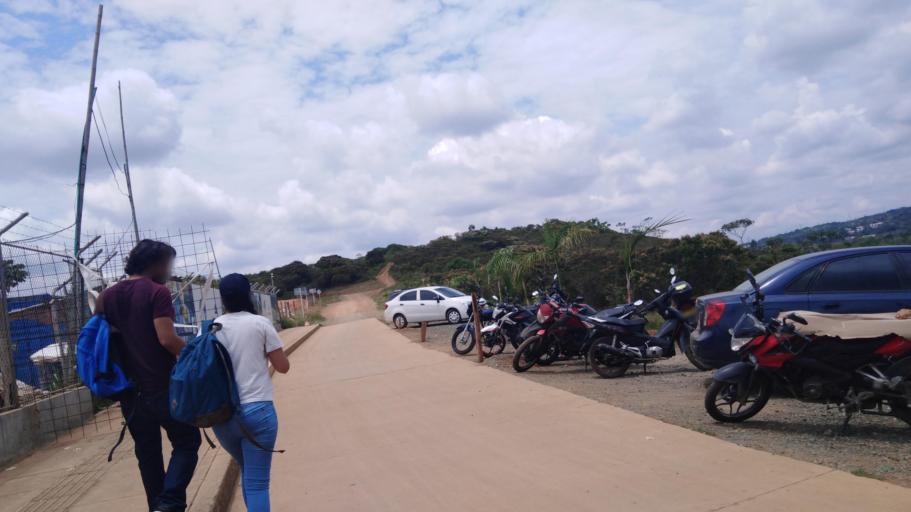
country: CO
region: Valle del Cauca
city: Cali
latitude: 3.3711
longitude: -76.5534
